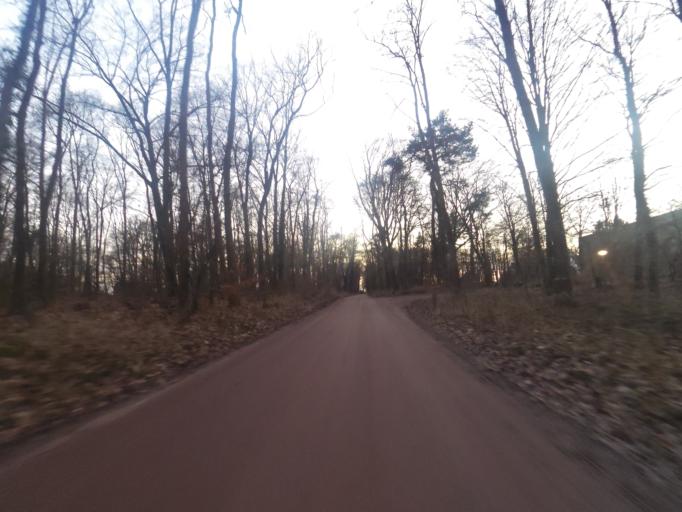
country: NL
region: Gelderland
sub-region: Gemeente Doetinchem
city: Doetinchem
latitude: 51.9387
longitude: 6.3312
